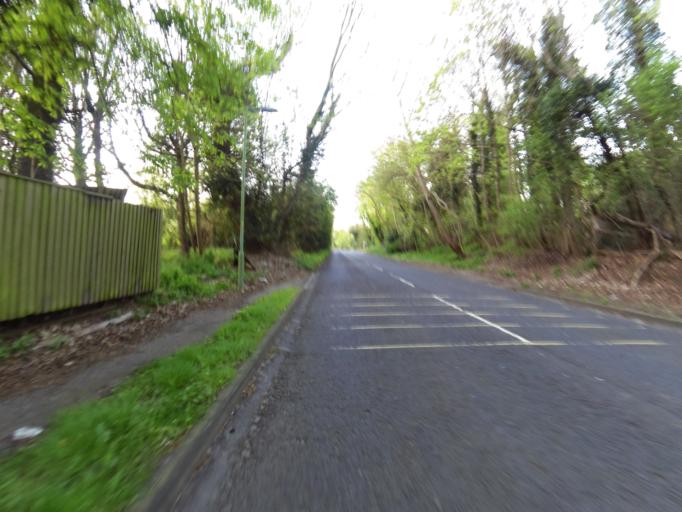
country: GB
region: England
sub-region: Suffolk
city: Bramford
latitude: 52.0586
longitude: 1.0955
